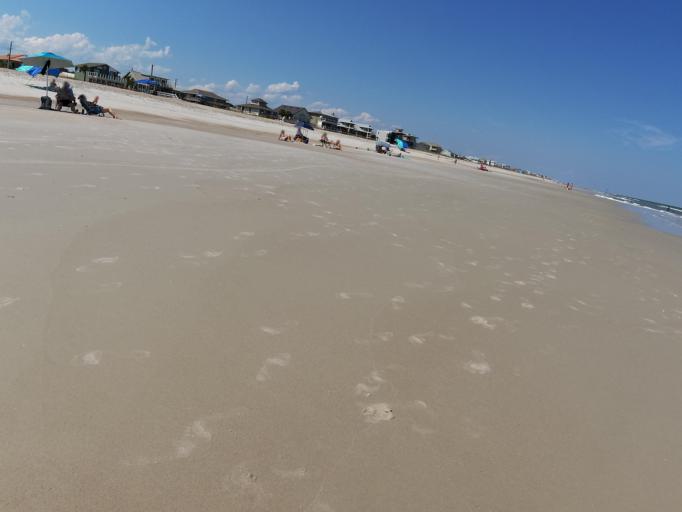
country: US
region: Florida
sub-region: Nassau County
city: Fernandina Beach
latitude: 30.6473
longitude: -81.4333
